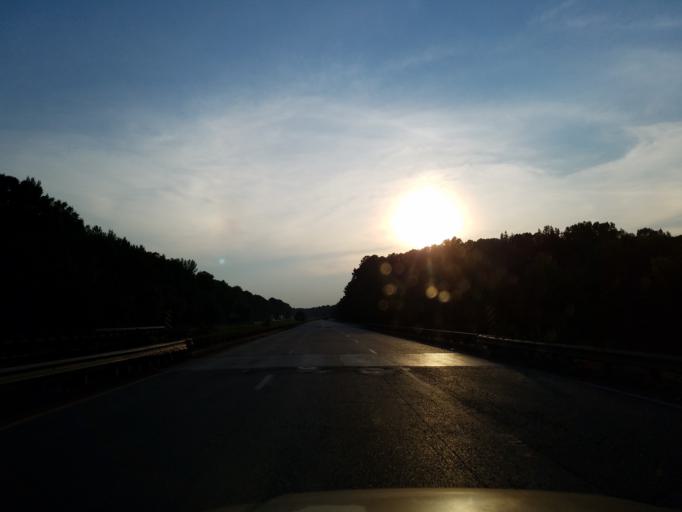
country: US
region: Mississippi
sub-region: Lauderdale County
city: Marion
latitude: 32.4136
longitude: -88.5083
